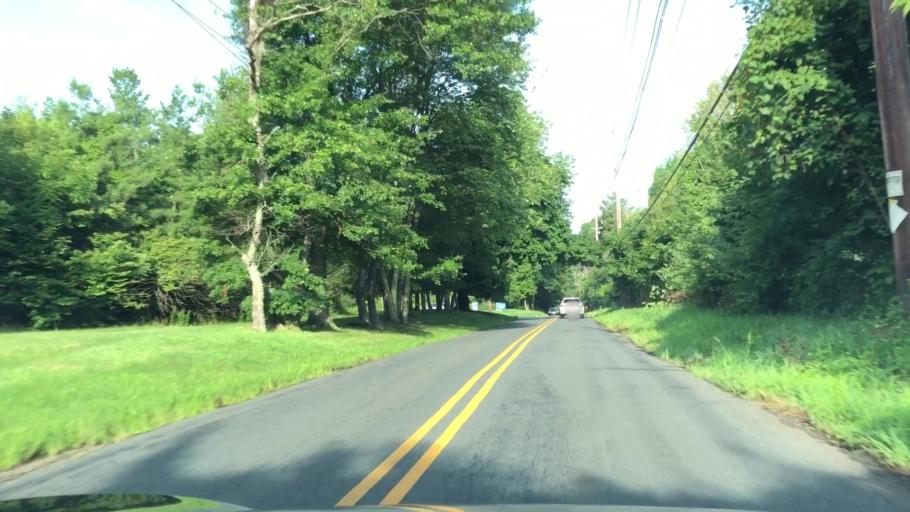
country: US
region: New Jersey
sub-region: Mercer County
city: Pennington
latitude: 40.3496
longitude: -74.7702
